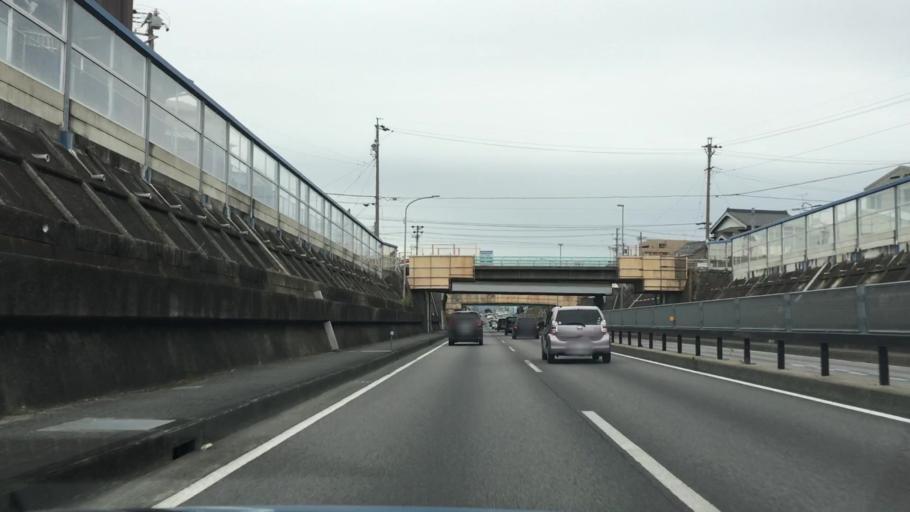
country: JP
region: Aichi
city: Kozakai-cho
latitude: 34.7988
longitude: 137.3657
